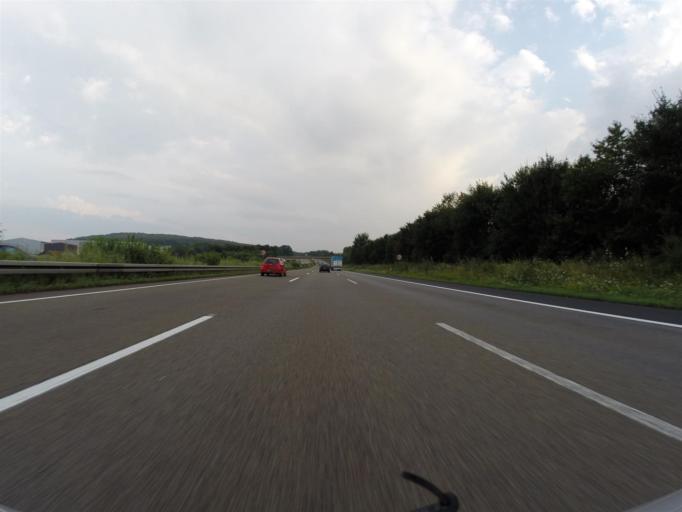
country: DE
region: Hesse
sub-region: Regierungsbezirk Kassel
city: Malsfeld
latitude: 51.0860
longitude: 9.4845
